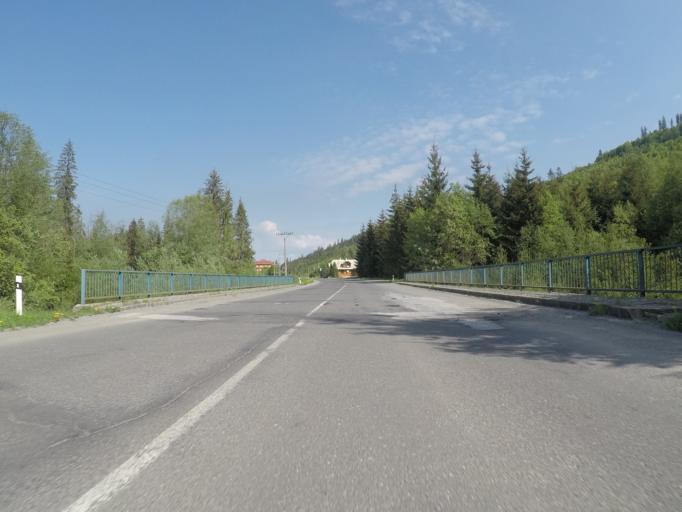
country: PL
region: Lesser Poland Voivodeship
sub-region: Powiat tatrzanski
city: Bukowina Tatrzanska
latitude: 49.2984
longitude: 20.1642
